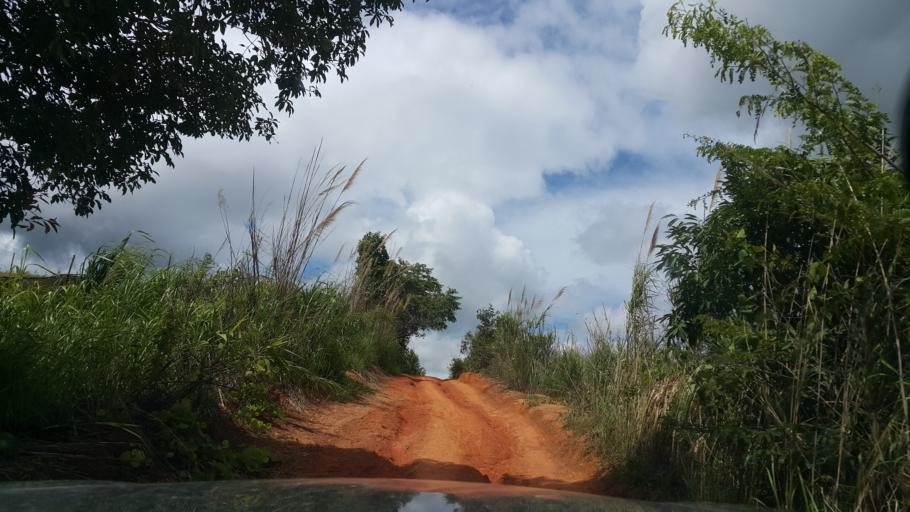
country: TH
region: Loei
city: Na Haeo
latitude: 17.5954
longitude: 100.9000
